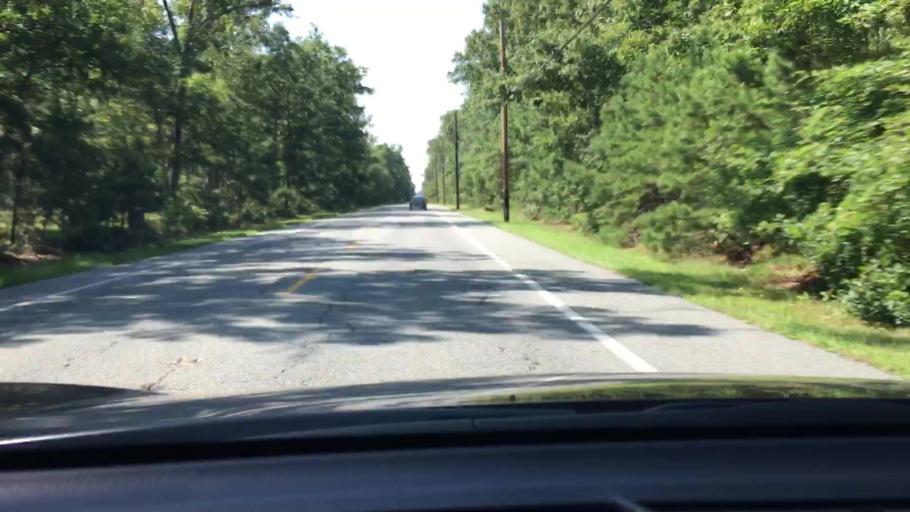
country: US
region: New Jersey
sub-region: Cape May County
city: Woodbine
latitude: 39.2761
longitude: -74.7965
